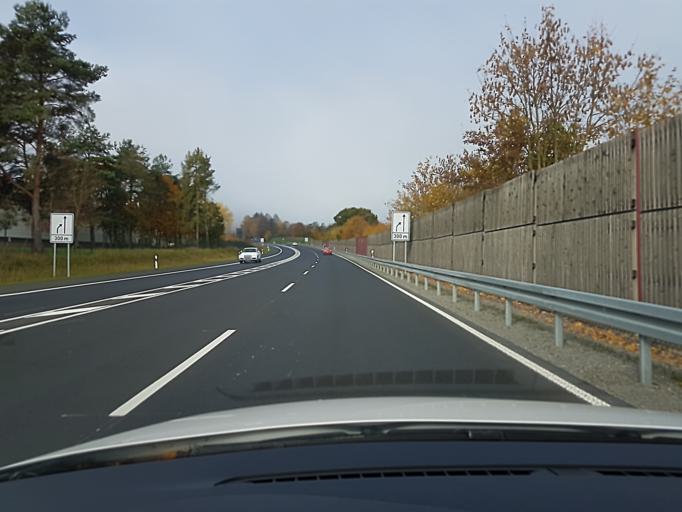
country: DE
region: Bavaria
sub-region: Regierungsbezirk Unterfranken
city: Kleinheubach
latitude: 49.7132
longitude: 9.2143
